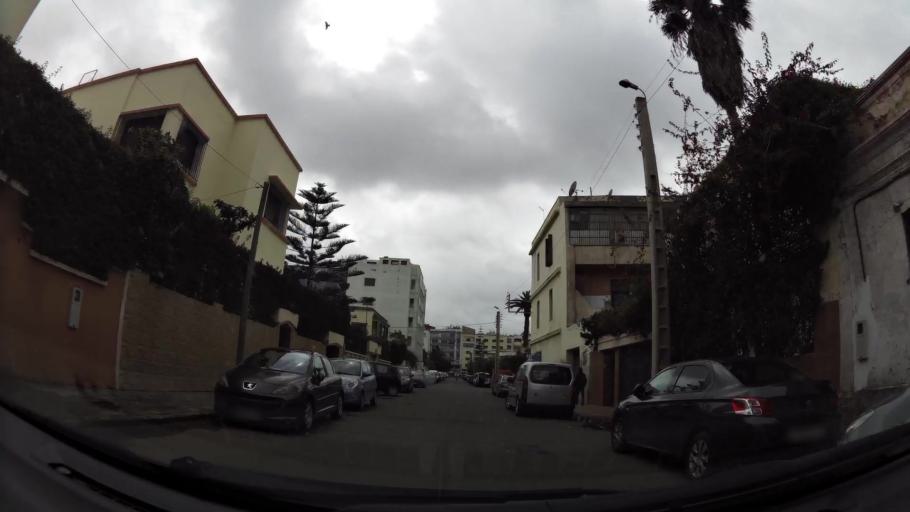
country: MA
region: Grand Casablanca
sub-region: Casablanca
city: Casablanca
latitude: 33.5826
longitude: -7.6122
